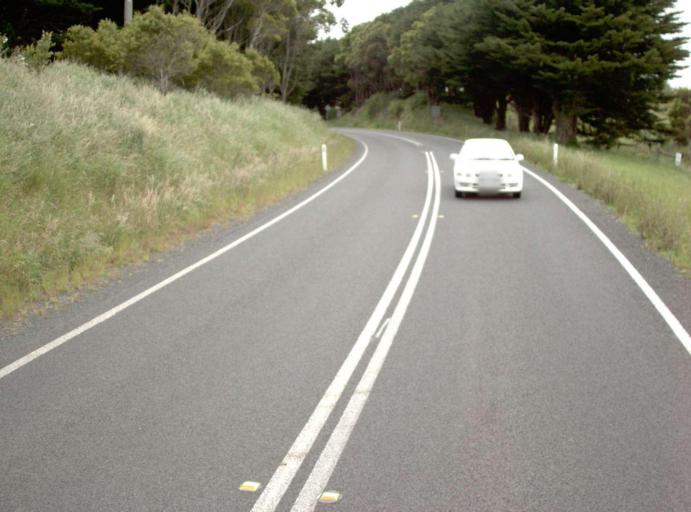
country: AU
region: Victoria
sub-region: Bass Coast
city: North Wonthaggi
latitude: -38.4907
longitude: 145.7455
